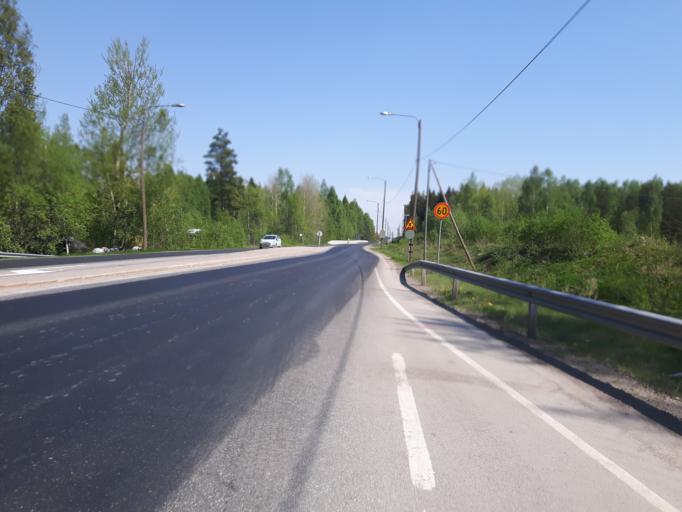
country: FI
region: Uusimaa
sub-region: Helsinki
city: Nickby
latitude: 60.3244
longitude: 25.4272
